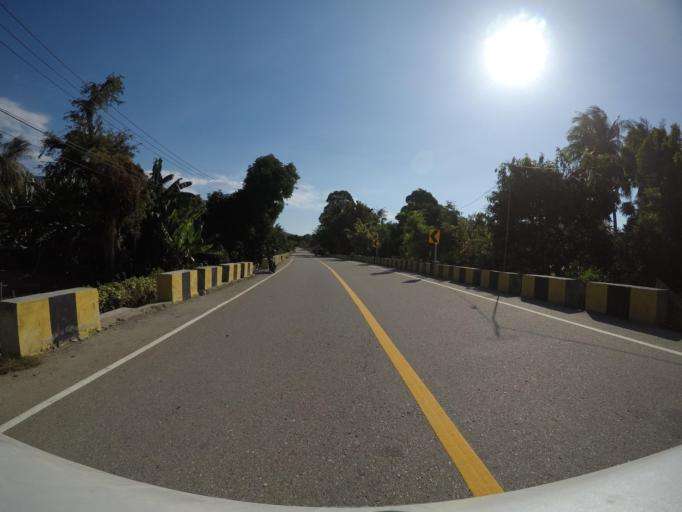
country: TL
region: Liquica
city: Maubara
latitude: -8.6193
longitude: 125.1739
